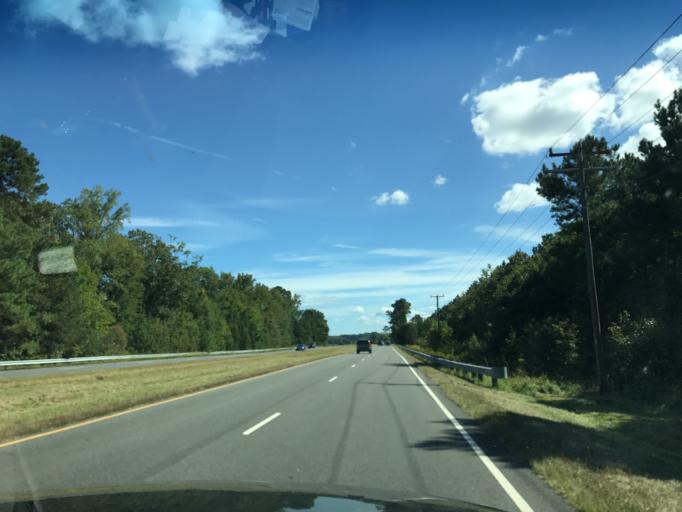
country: US
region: Virginia
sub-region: Essex County
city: Tappahannock
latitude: 37.8848
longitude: -76.8618
